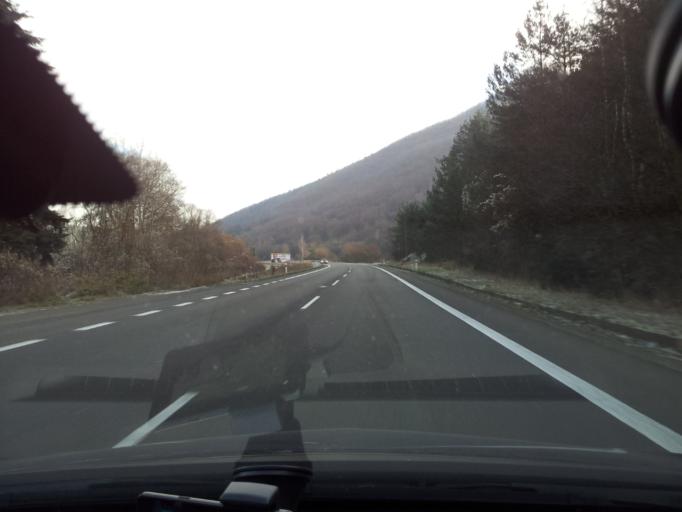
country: SK
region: Banskobystricky
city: Hrochot,Slovakia
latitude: 48.7743
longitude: 19.3037
